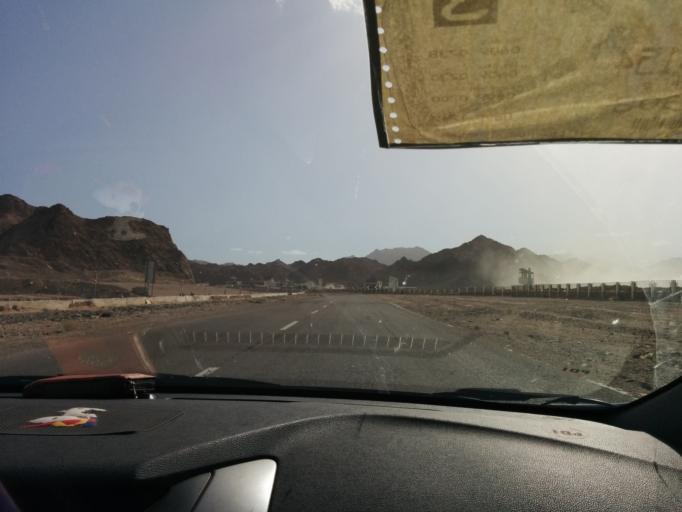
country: EG
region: South Sinai
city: Sharm el-Sheikh
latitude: 28.1749
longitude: 34.3096
